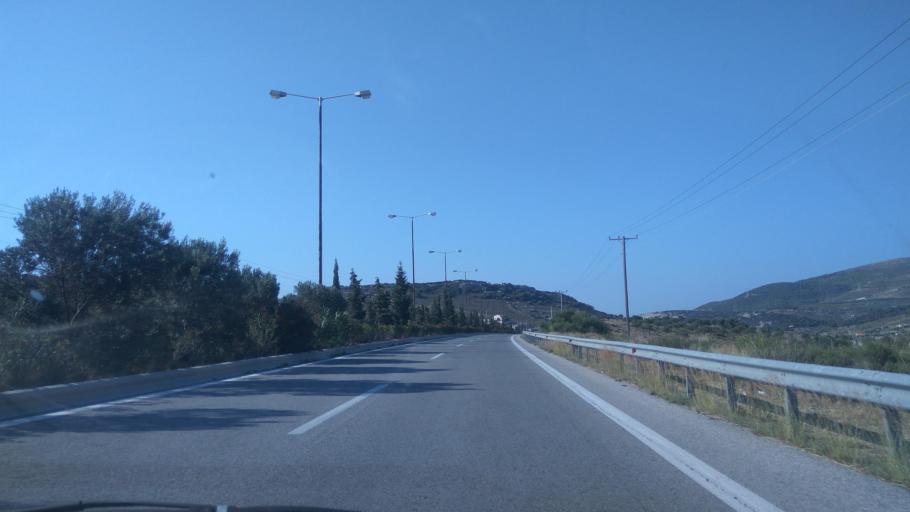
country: GR
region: Attica
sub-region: Nomarchia Anatolikis Attikis
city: Lavrio
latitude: 37.7853
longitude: 24.0575
